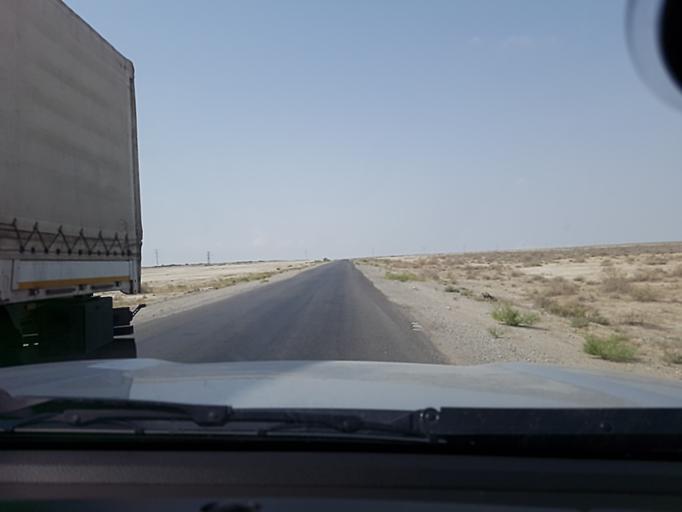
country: TM
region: Balkan
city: Gumdag
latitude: 38.7704
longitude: 54.5871
